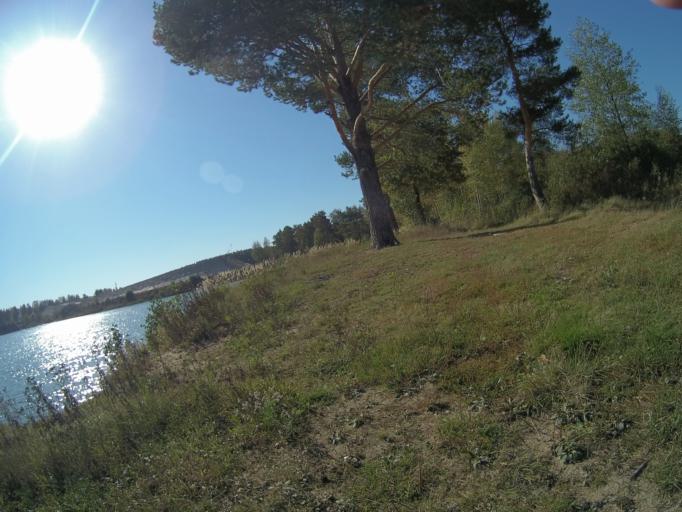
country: RU
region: Vladimir
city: Raduzhnyy
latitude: 56.0326
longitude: 40.3269
